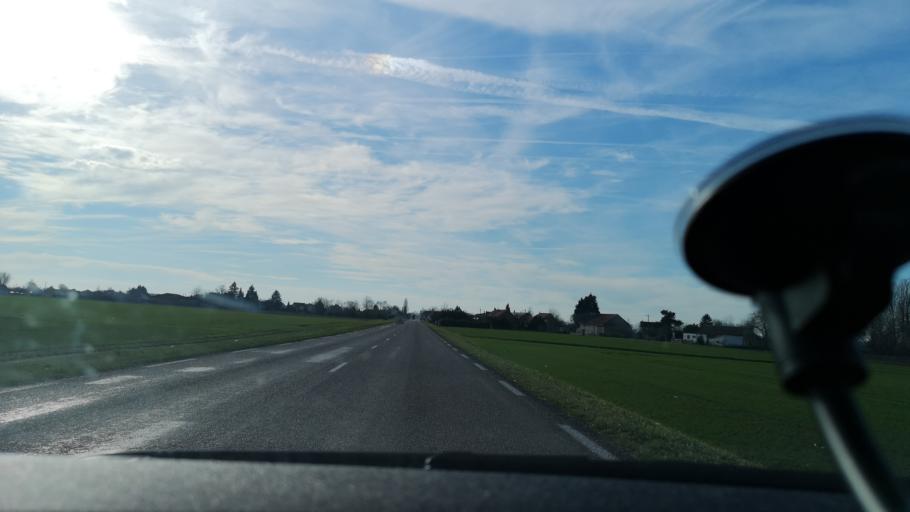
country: FR
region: Franche-Comte
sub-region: Departement du Jura
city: Petit-Noir
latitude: 46.9718
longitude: 5.3037
